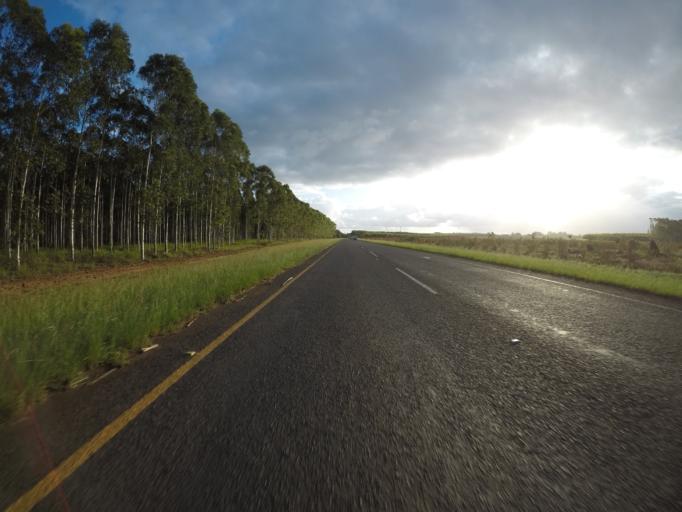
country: ZA
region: KwaZulu-Natal
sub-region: uMkhanyakude District Municipality
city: Mtubatuba
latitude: -28.4091
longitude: 32.1974
